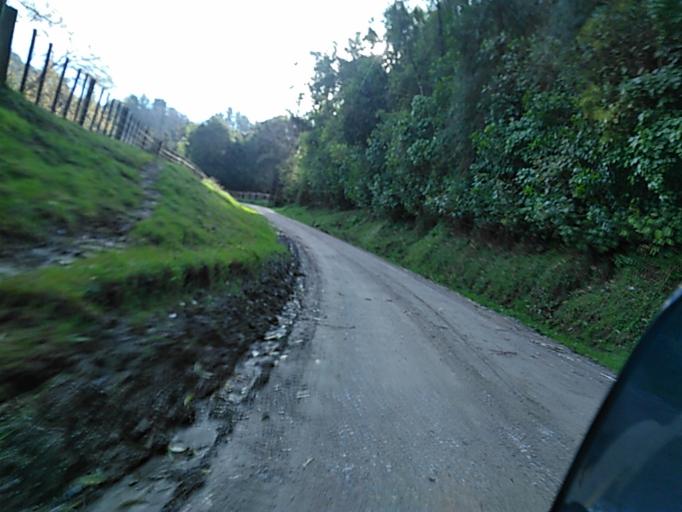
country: NZ
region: Gisborne
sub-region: Gisborne District
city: Gisborne
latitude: -38.5883
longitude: 178.0688
